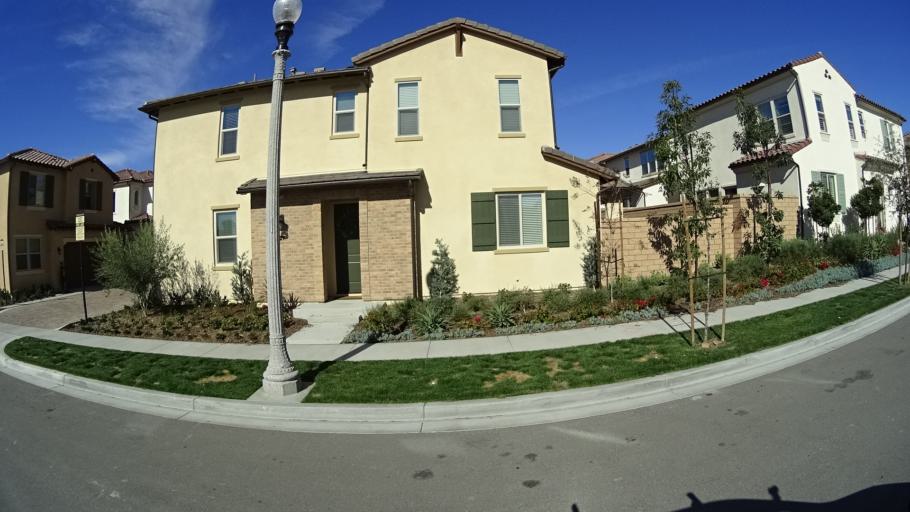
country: US
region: California
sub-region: Orange County
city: Foothill Ranch
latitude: 33.6790
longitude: -117.6804
